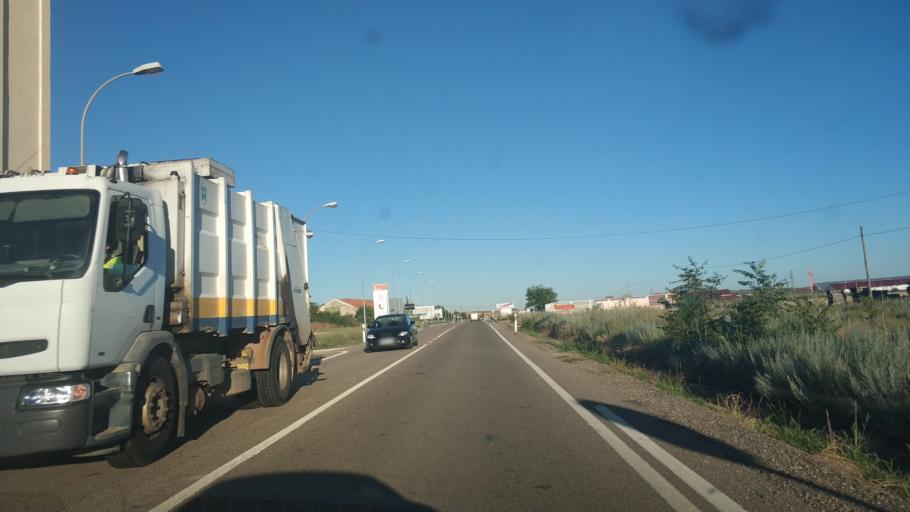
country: ES
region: Castille and Leon
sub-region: Provincia de Soria
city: San Esteban de Gormaz
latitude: 41.5689
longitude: -3.1919
